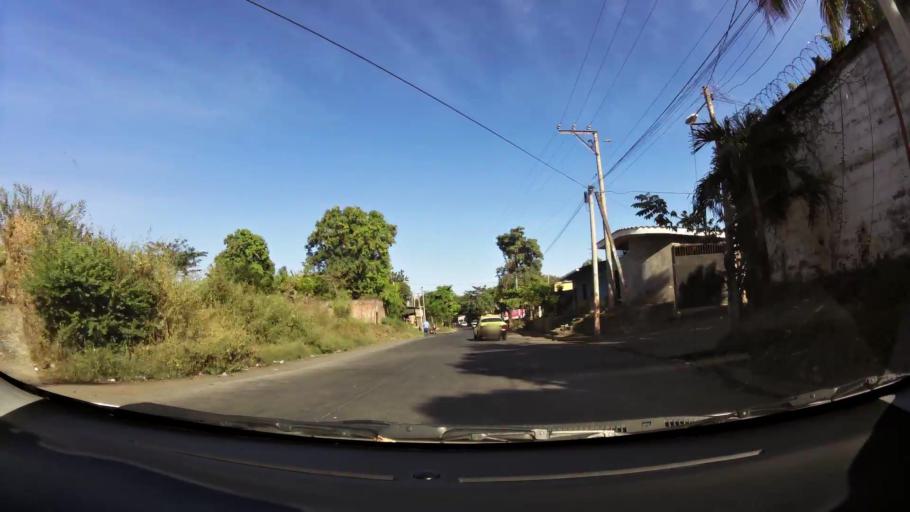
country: SV
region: San Miguel
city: San Miguel
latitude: 13.4775
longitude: -88.1938
